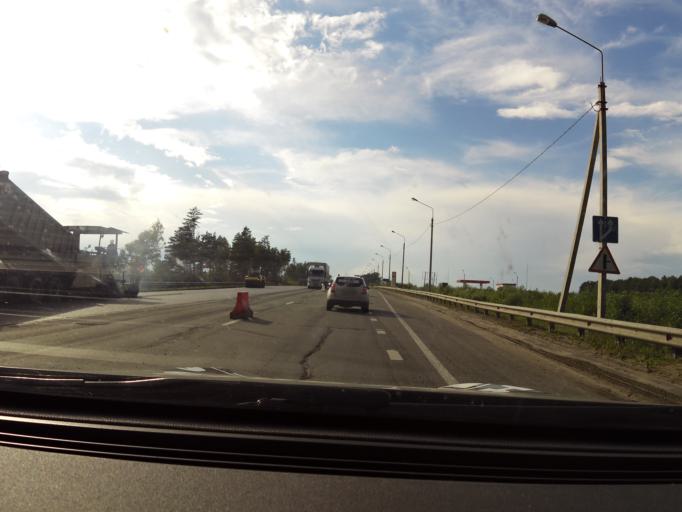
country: RU
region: Vladimir
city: Novovyazniki
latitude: 56.1845
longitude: 42.4005
